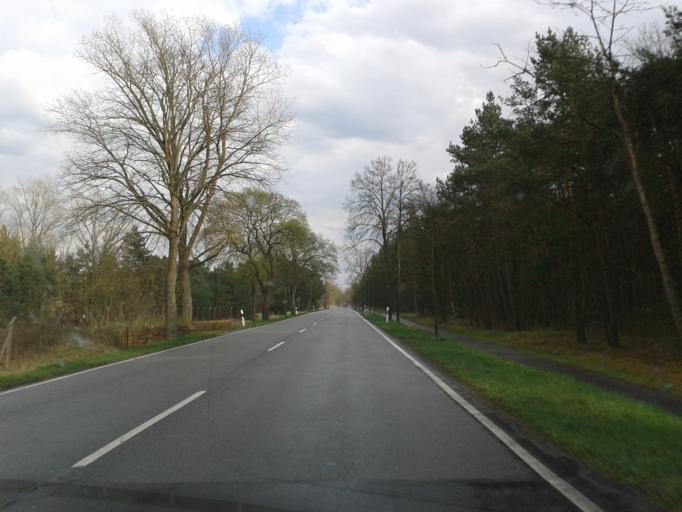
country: DE
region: Lower Saxony
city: Bergen an der Dumme
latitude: 52.8827
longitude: 11.0151
